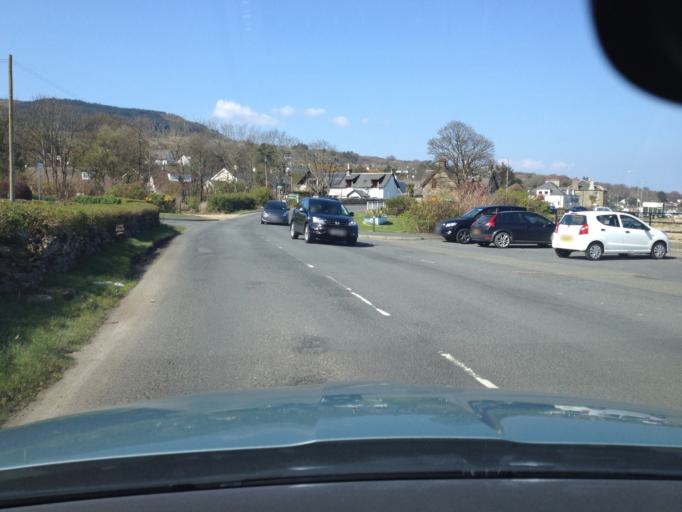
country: GB
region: Scotland
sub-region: North Ayrshire
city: Lamlash
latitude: 55.4818
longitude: -5.0921
